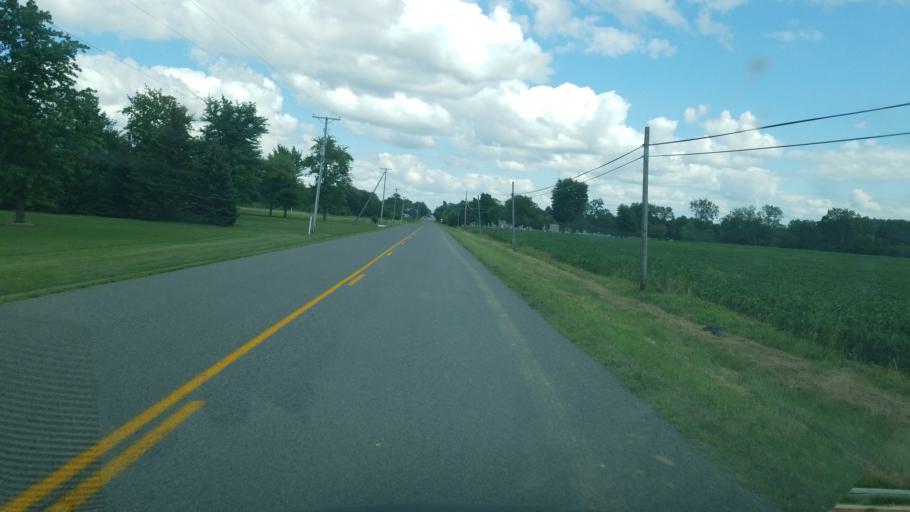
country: US
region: Ohio
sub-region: Allen County
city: Lima
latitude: 40.8318
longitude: -84.1001
